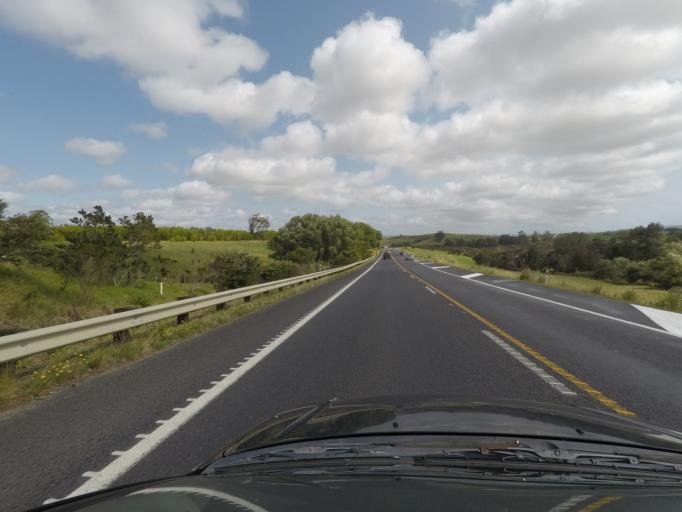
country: NZ
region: Northland
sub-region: Whangarei
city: Ruakaka
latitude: -35.8491
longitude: 174.3502
